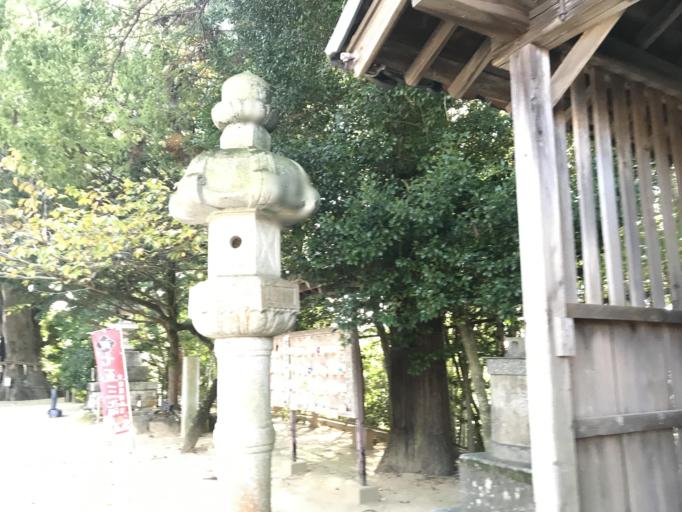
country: JP
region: Ibaraki
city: Ishioka
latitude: 36.1881
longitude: 140.2689
